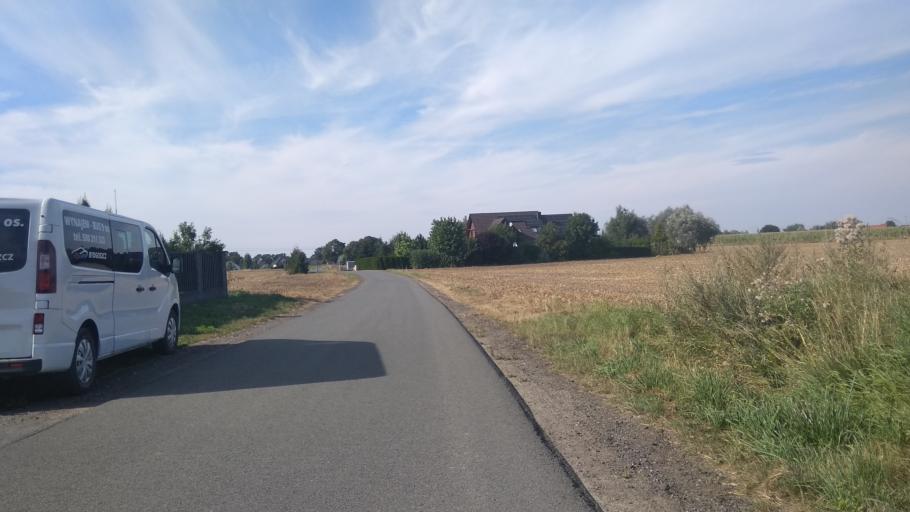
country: PL
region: Kujawsko-Pomorskie
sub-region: Powiat bydgoski
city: Osielsko
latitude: 53.2204
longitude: 18.1458
